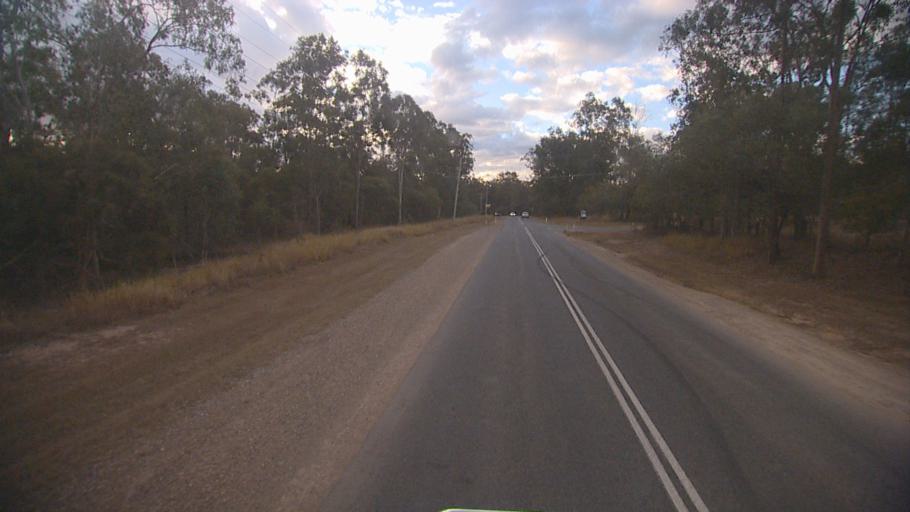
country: AU
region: Queensland
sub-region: Logan
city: Cedar Vale
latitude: -27.8408
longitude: 153.0481
